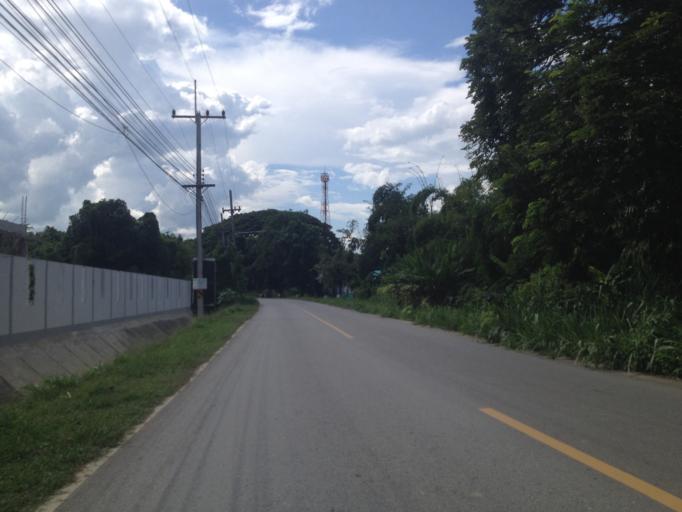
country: TH
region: Chiang Mai
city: Hang Dong
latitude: 18.7107
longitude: 98.9440
